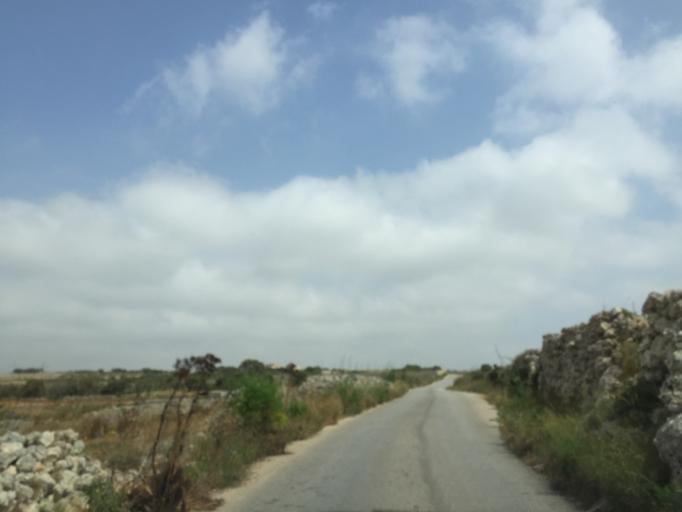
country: MT
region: L-Imgarr
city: Imgarr
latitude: 35.8955
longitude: 14.3581
